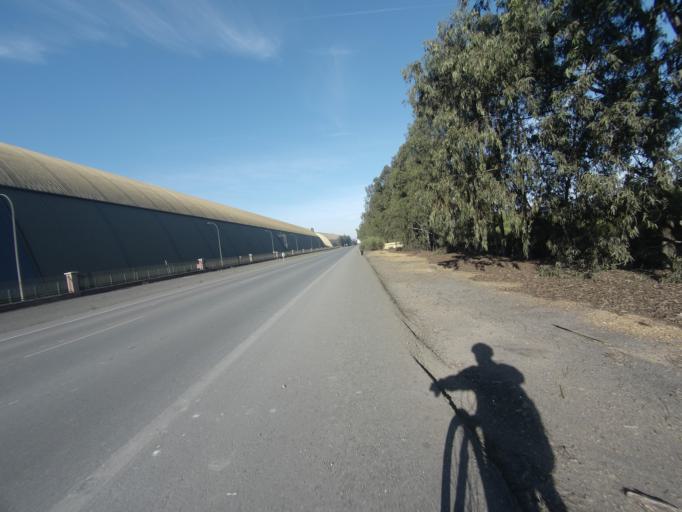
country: ES
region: Andalusia
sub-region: Provincia de Huelva
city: Punta Umbria
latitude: 37.1811
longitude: -6.9215
